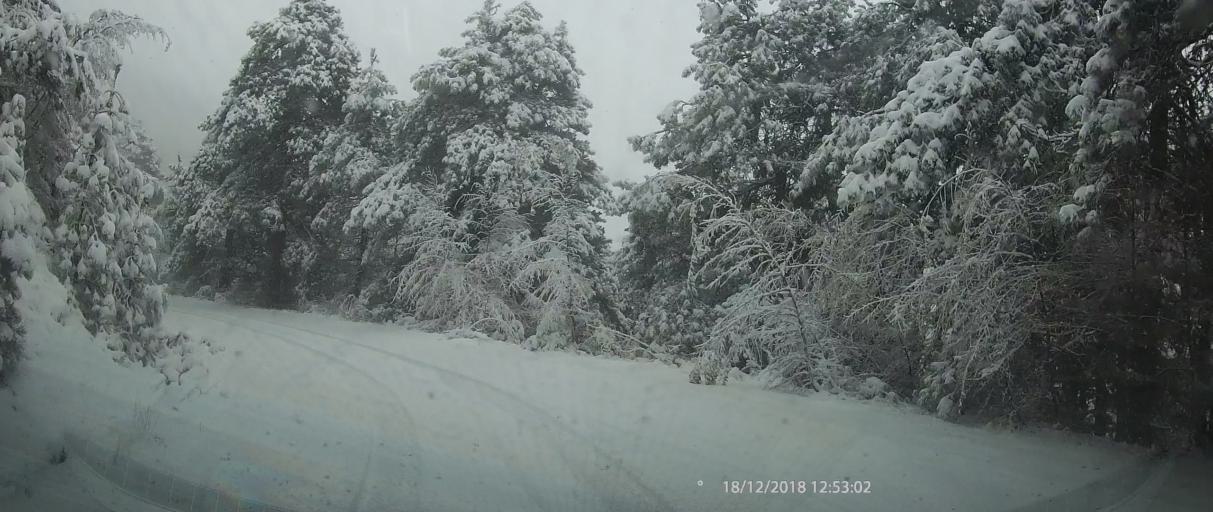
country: GR
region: Central Macedonia
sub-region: Nomos Pierias
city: Litochoro
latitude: 40.1031
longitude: 22.4532
